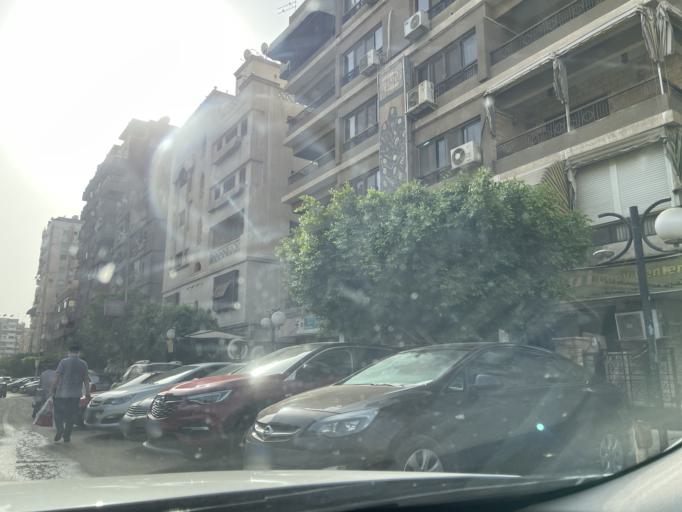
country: EG
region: Muhafazat al Qahirah
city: Cairo
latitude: 30.0659
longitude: 31.3524
